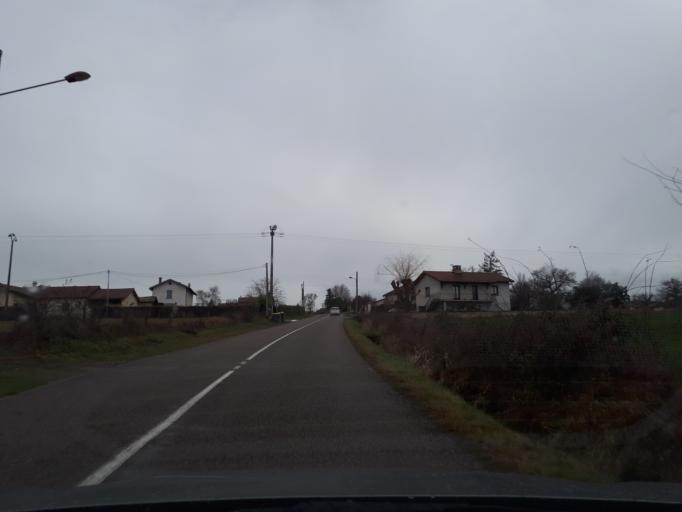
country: FR
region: Rhone-Alpes
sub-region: Departement de la Loire
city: Boen-sur-Lignon
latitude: 45.7750
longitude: 4.0269
